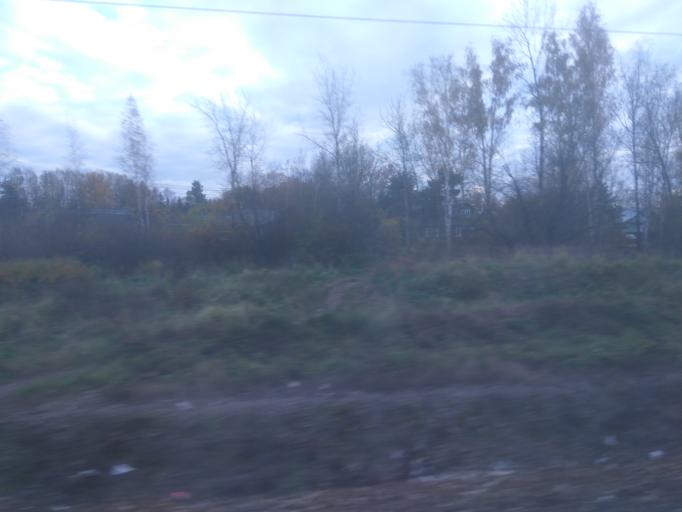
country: RU
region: Moskovskaya
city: Kokoshkino
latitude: 55.5957
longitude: 37.1617
